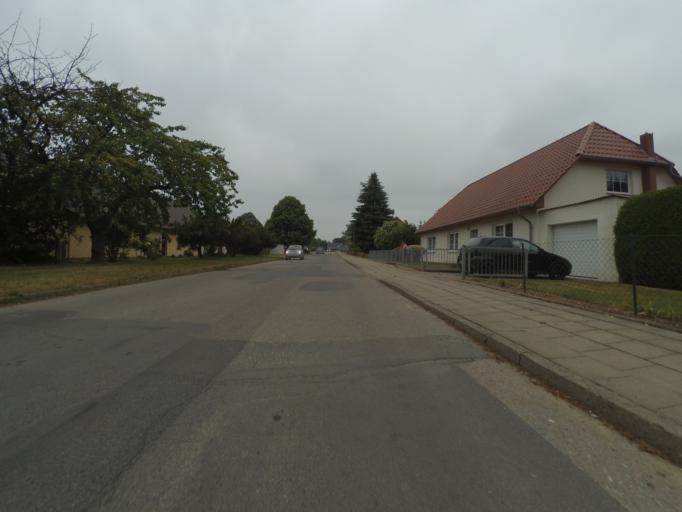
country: DE
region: Mecklenburg-Vorpommern
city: Plau am See
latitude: 53.4959
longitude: 12.2140
